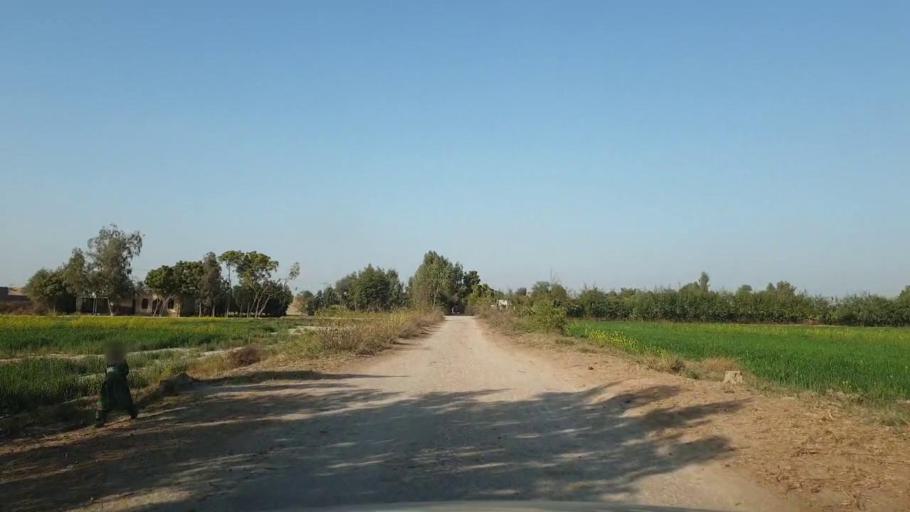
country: PK
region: Sindh
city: Tando Allahyar
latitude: 25.5107
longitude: 68.6551
